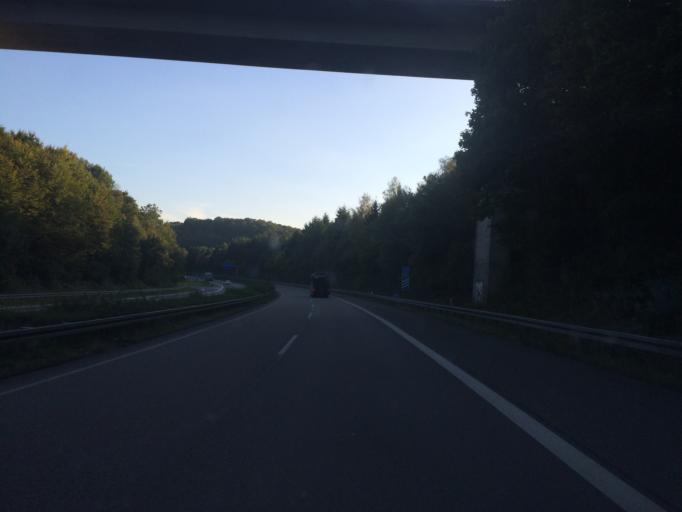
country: DE
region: Saarland
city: Tholey
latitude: 49.4928
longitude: 6.9878
